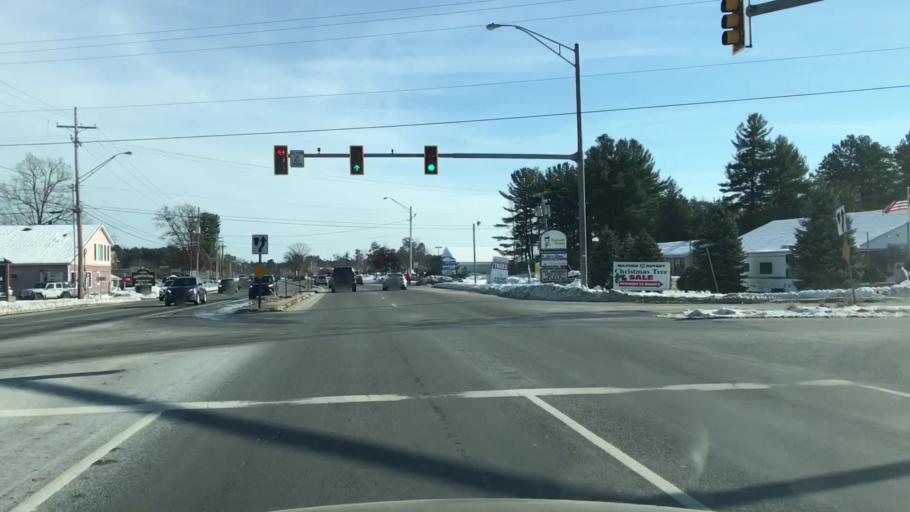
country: US
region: New Hampshire
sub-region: Hillsborough County
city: Hollis
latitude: 42.8094
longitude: -71.5734
